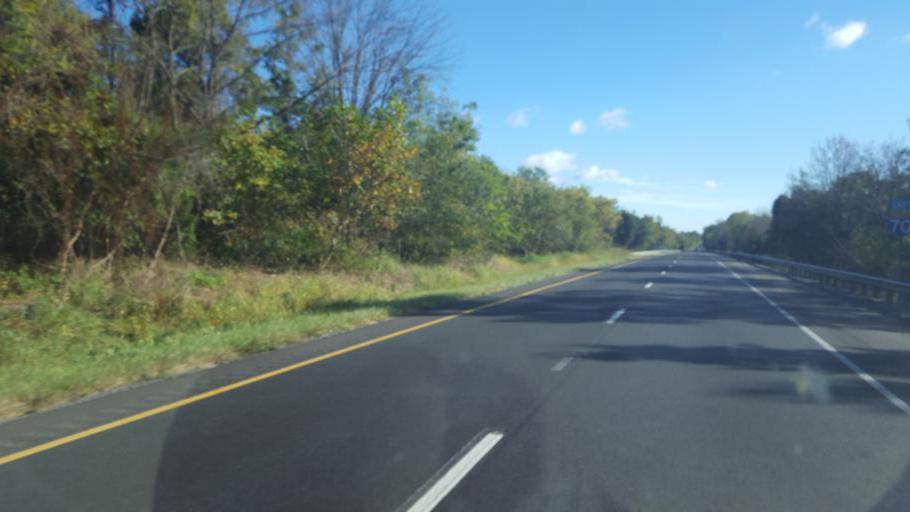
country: US
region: Maryland
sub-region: Washington County
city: Wilson-Conococheague
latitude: 39.6330
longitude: -77.9605
